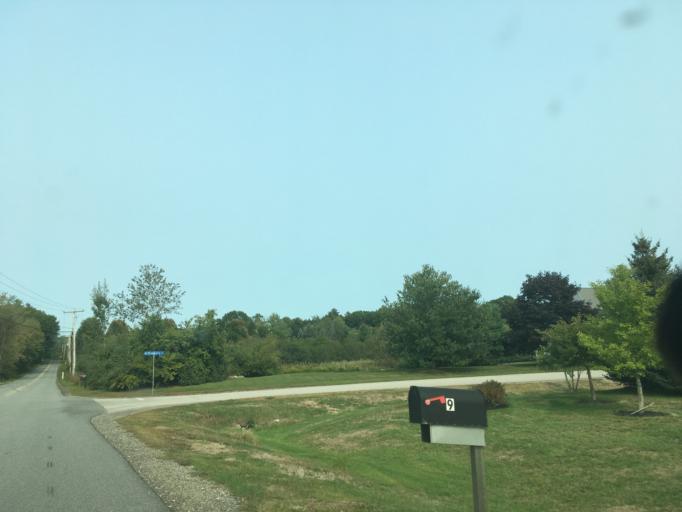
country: US
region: New Hampshire
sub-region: Rockingham County
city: Stratham Station
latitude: 42.9996
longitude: -70.8850
